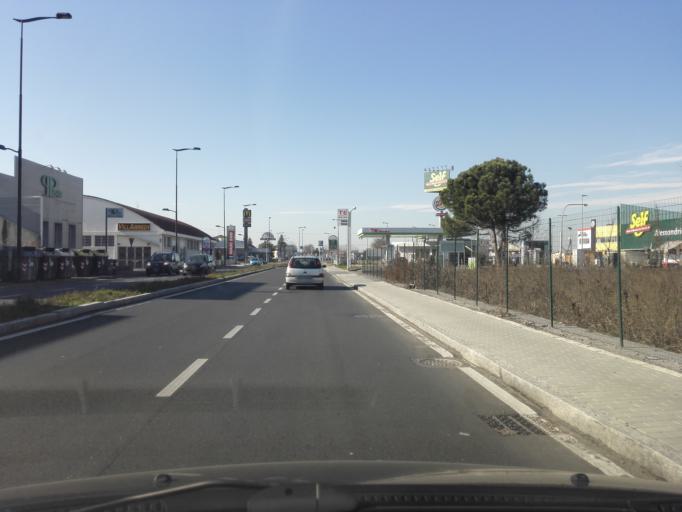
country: IT
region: Piedmont
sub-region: Provincia di Alessandria
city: Alessandria
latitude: 44.9194
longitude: 8.5960
